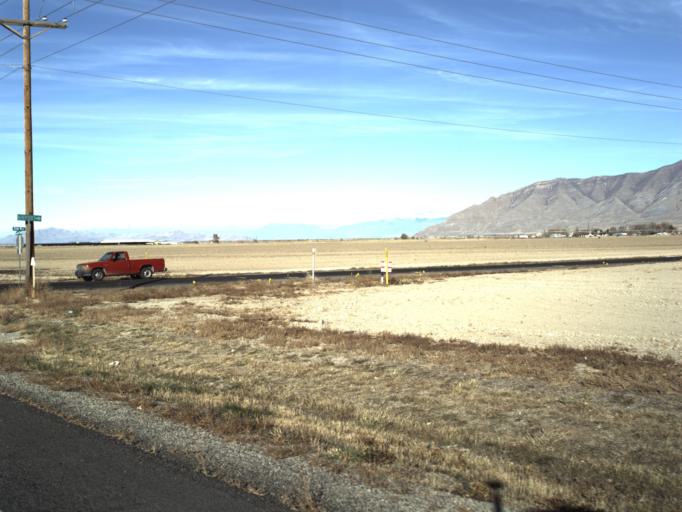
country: US
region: Utah
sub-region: Tooele County
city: Erda
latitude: 40.6006
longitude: -112.3706
